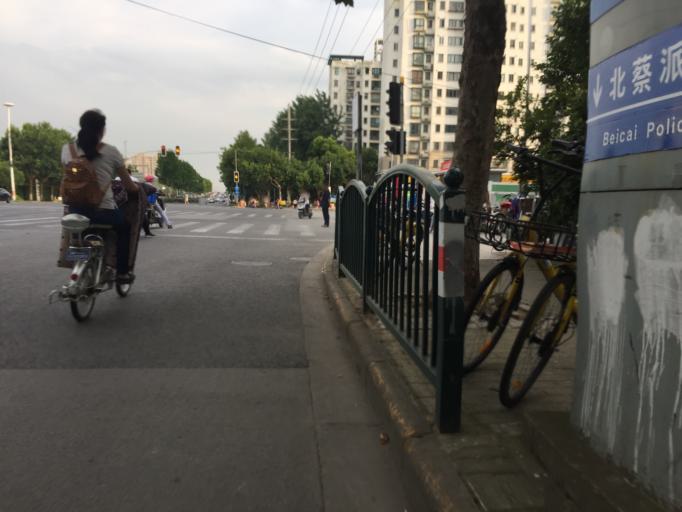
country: CN
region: Shanghai Shi
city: Huamu
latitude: 31.1823
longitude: 121.5374
